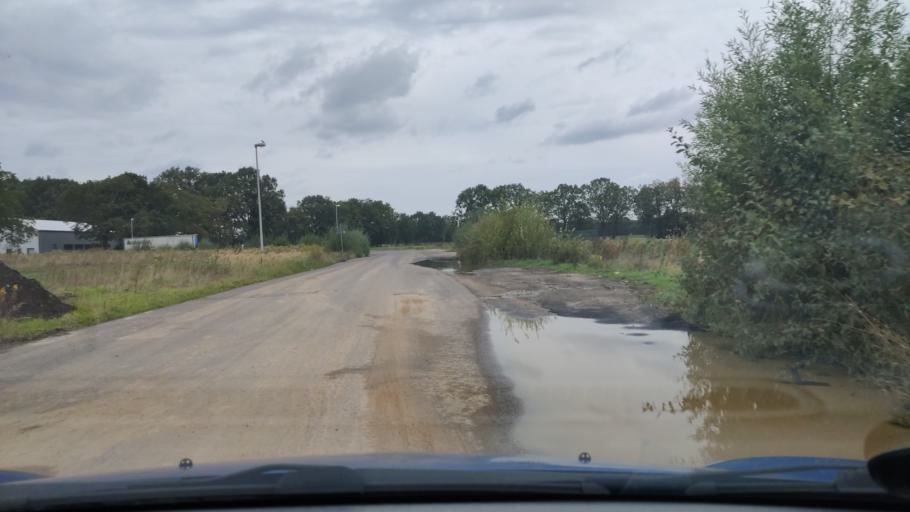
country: DE
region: Lower Saxony
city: Garbsen-Mitte
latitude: 52.4310
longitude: 9.6651
